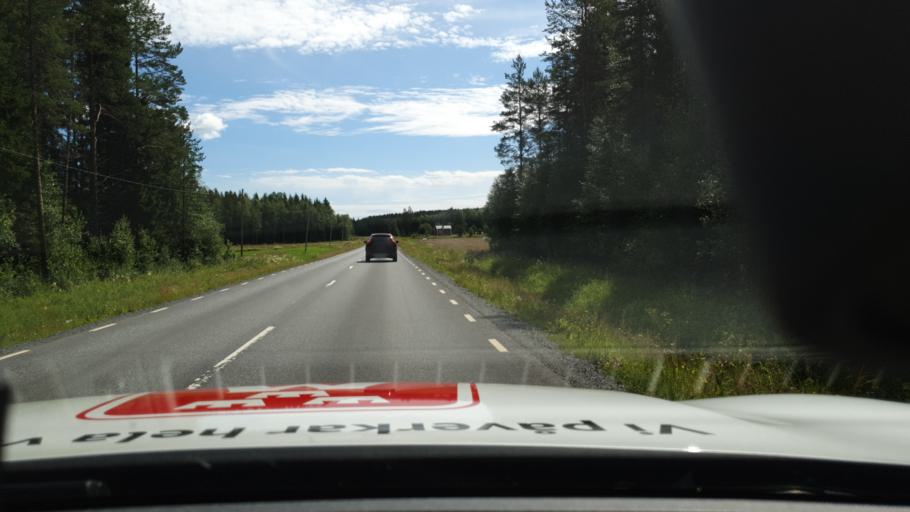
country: SE
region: Norrbotten
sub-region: Lulea Kommun
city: Ranea
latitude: 65.7871
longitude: 22.1567
